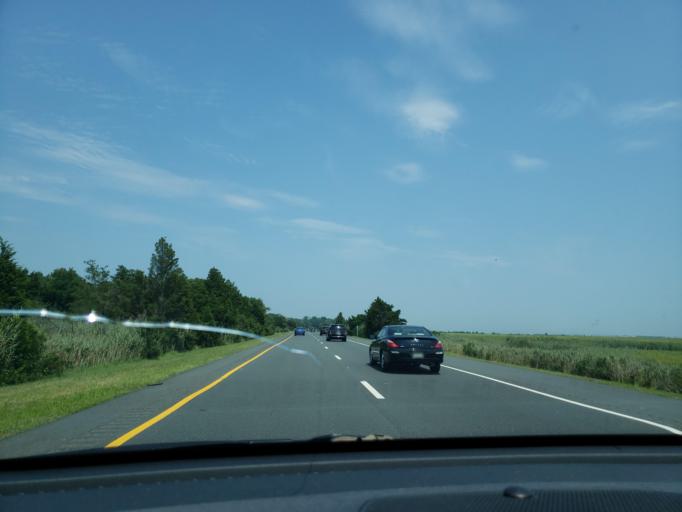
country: US
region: New Jersey
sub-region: Cape May County
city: Sea Isle City
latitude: 39.2257
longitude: -74.6761
